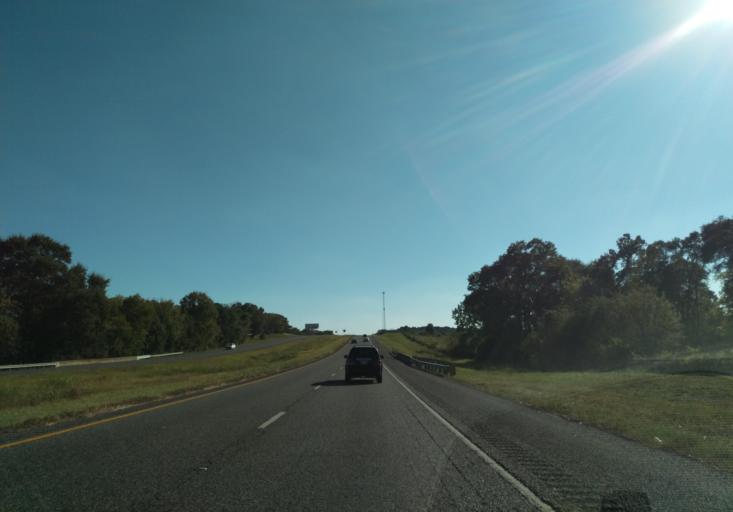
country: US
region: Texas
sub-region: Waller County
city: Hempstead
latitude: 30.1800
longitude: -96.0645
